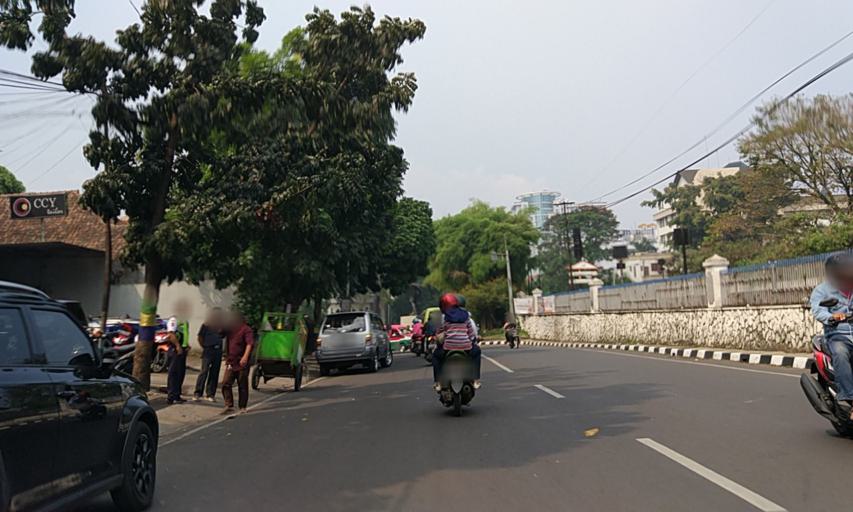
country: ID
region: West Java
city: Bandung
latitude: -6.9147
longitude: 107.6063
